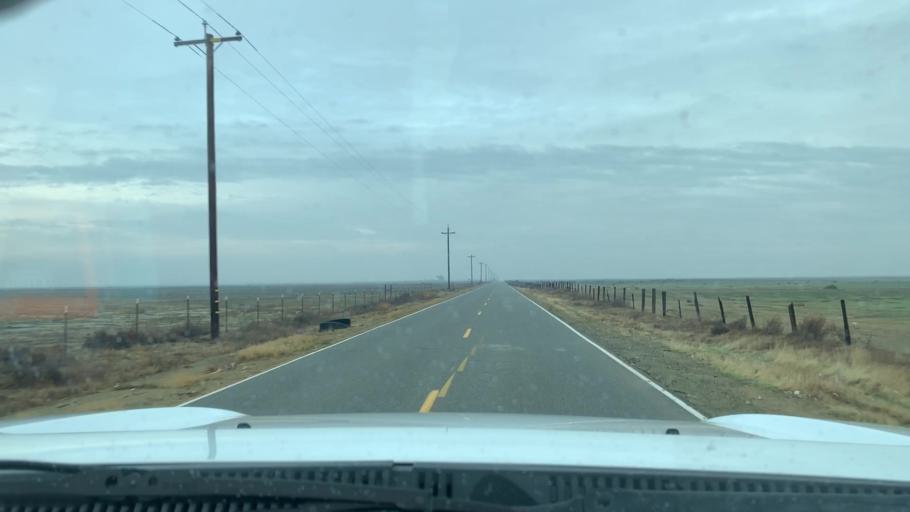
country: US
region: California
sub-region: Kern County
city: Lost Hills
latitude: 35.6849
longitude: -119.5798
